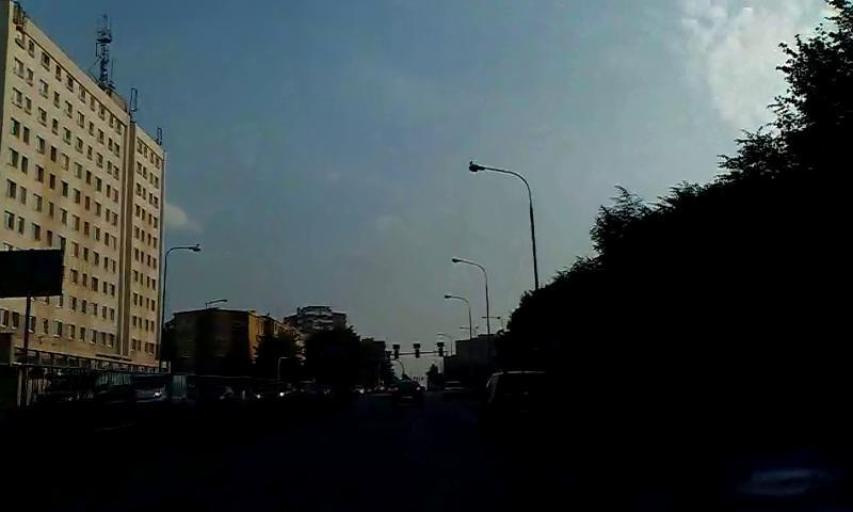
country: PL
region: Lublin Voivodeship
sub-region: Powiat lubelski
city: Lublin
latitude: 51.2352
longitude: 22.5944
